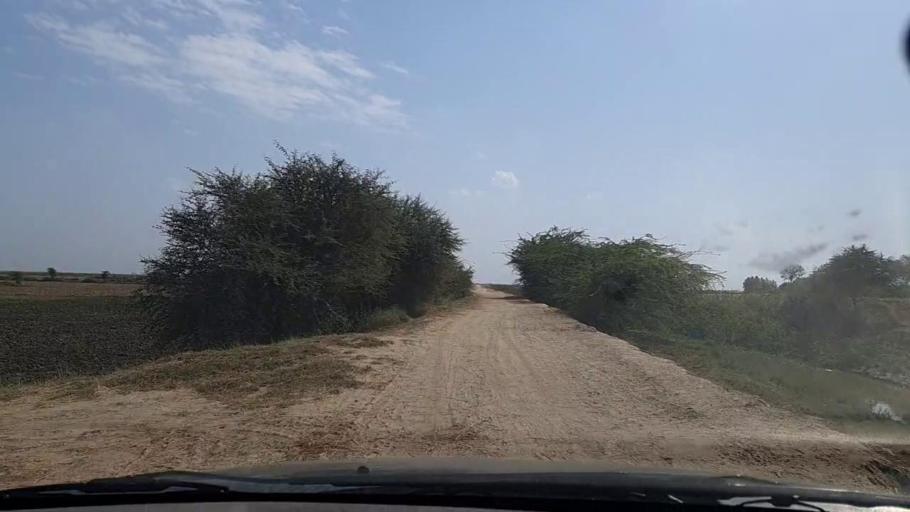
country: PK
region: Sindh
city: Mirpur Batoro
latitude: 24.5570
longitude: 68.2010
